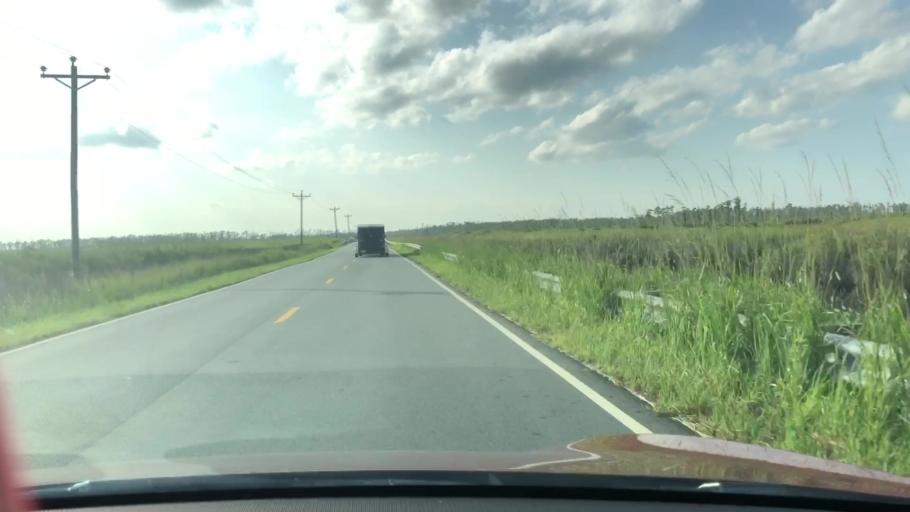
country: US
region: North Carolina
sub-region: Dare County
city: Wanchese
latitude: 35.6301
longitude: -75.8531
